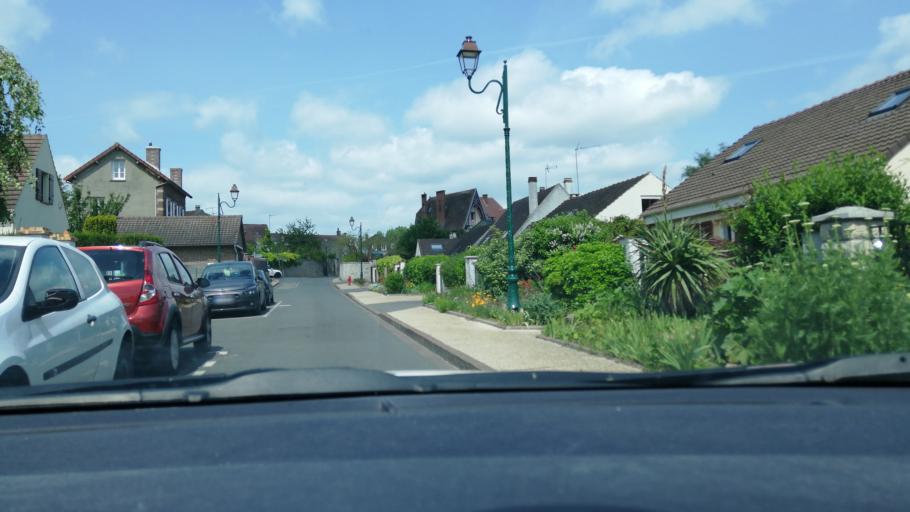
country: FR
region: Ile-de-France
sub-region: Departement du Val-d'Oise
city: Osny
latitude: 49.0724
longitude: 2.0281
